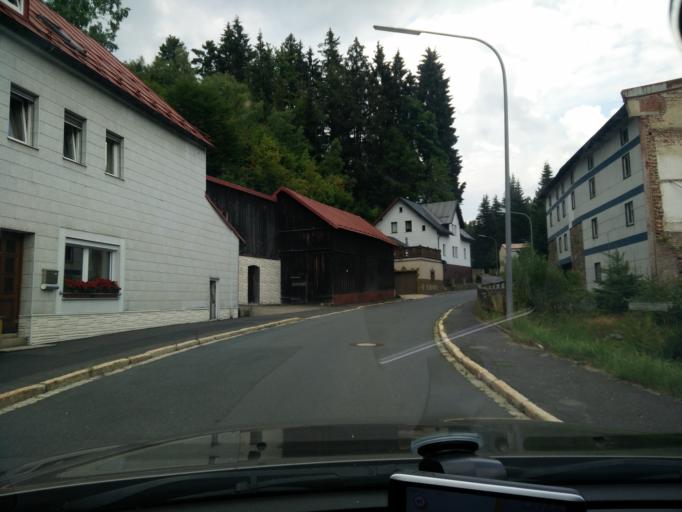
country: DE
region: Bavaria
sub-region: Upper Franconia
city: Fichtelberg
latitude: 50.0032
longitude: 11.8519
